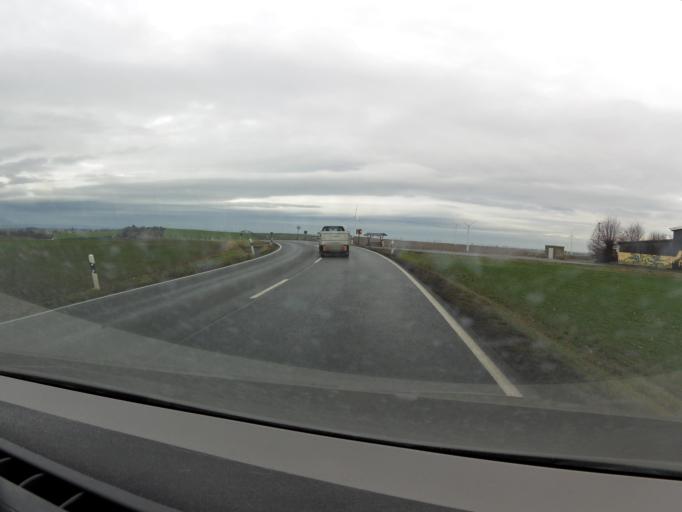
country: DE
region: Saxony-Anhalt
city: Hettstedt
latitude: 51.6730
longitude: 11.4633
